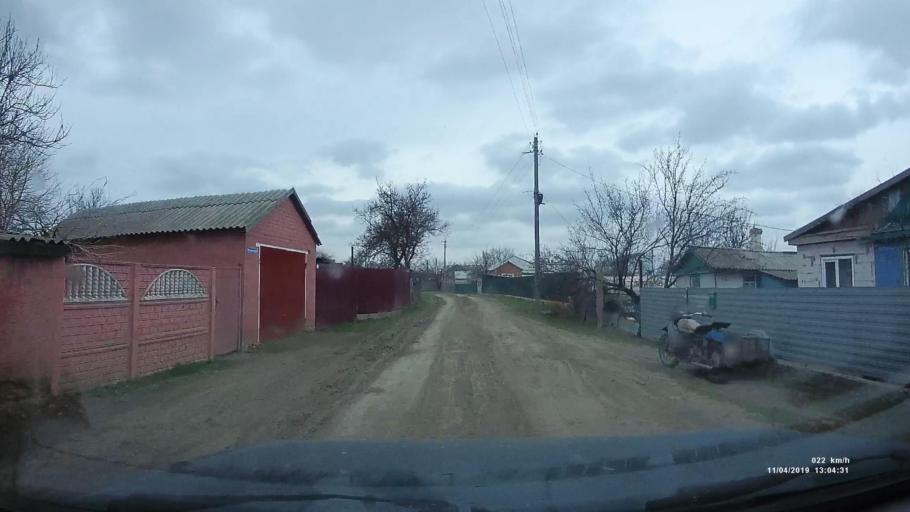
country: RU
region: Rostov
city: Staraya Stanitsa
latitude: 48.2872
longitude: 40.3465
